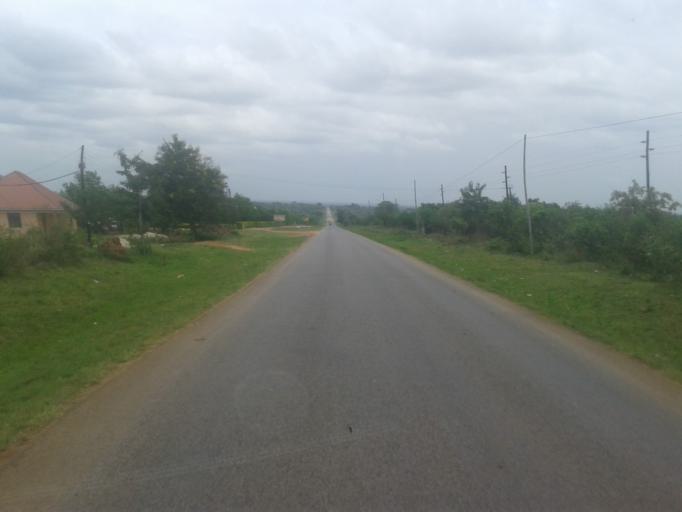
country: UG
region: Western Region
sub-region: Kiryandongo District
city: Masindi Port
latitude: 1.5115
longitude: 32.0829
